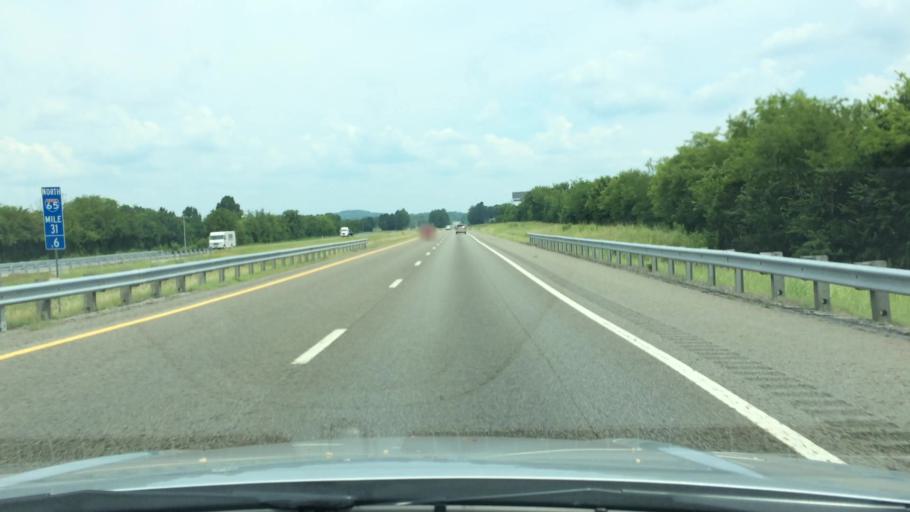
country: US
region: Tennessee
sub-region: Marshall County
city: Cornersville
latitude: 35.4357
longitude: -86.8808
